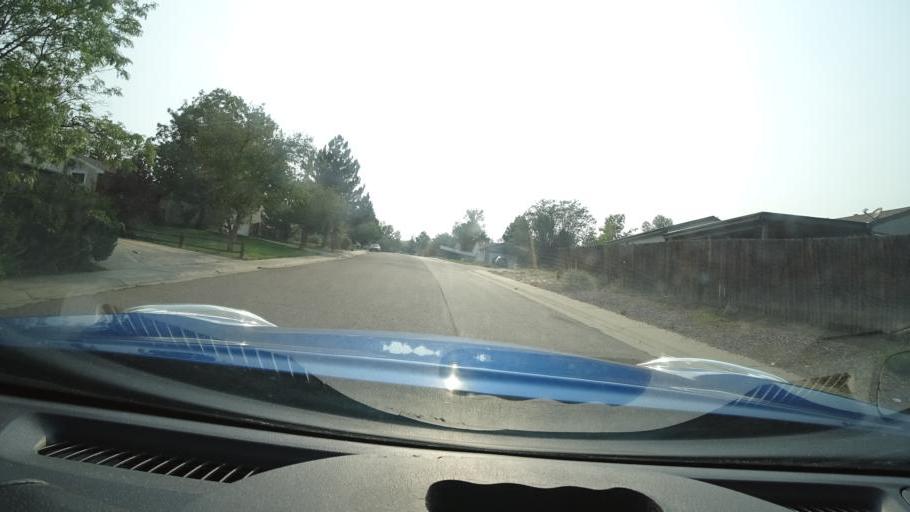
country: US
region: Colorado
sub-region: Adams County
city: Aurora
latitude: 39.6648
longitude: -104.7805
